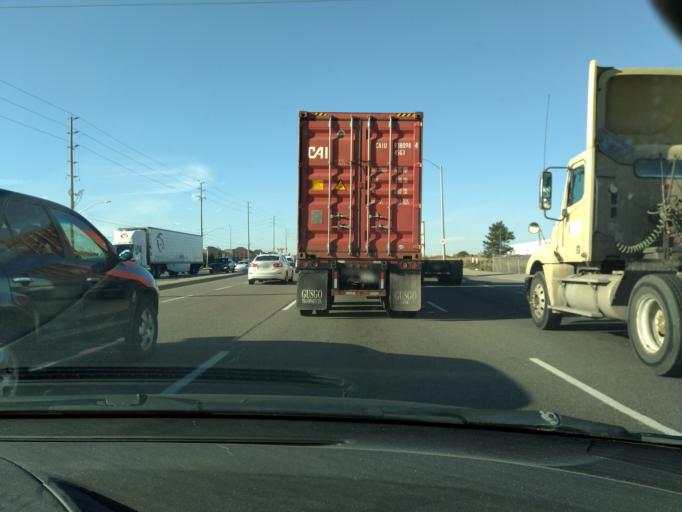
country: CA
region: Ontario
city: Brampton
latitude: 43.7769
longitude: -79.6540
